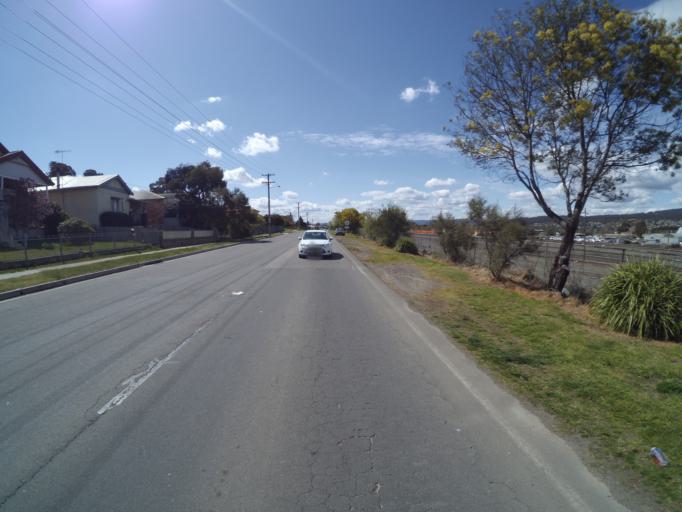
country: AU
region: New South Wales
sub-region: Goulburn Mulwaree
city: Goulburn
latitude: -34.7686
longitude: 149.7113
